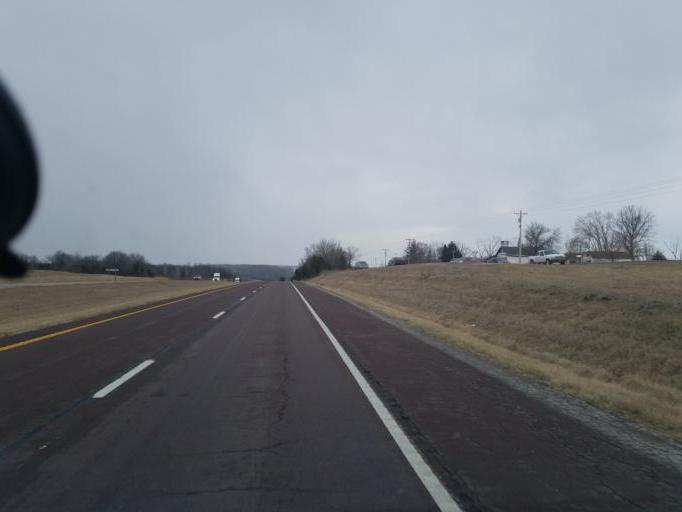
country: US
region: Missouri
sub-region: Boone County
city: Hallsville
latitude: 39.1379
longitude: -92.3325
